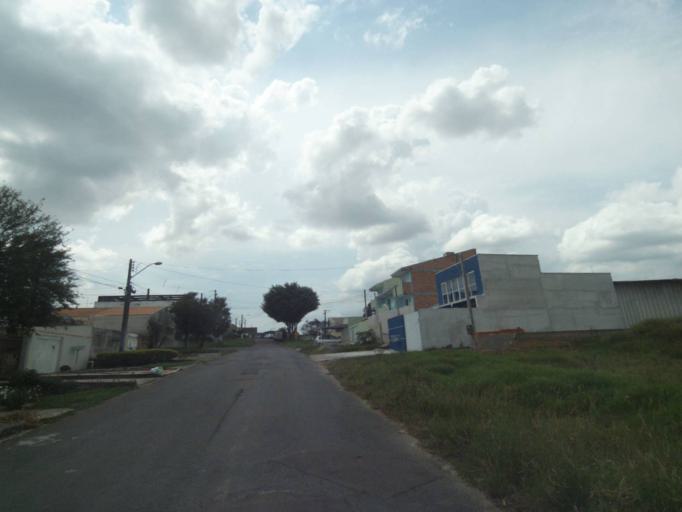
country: BR
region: Parana
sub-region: Pinhais
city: Pinhais
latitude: -25.3947
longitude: -49.1992
